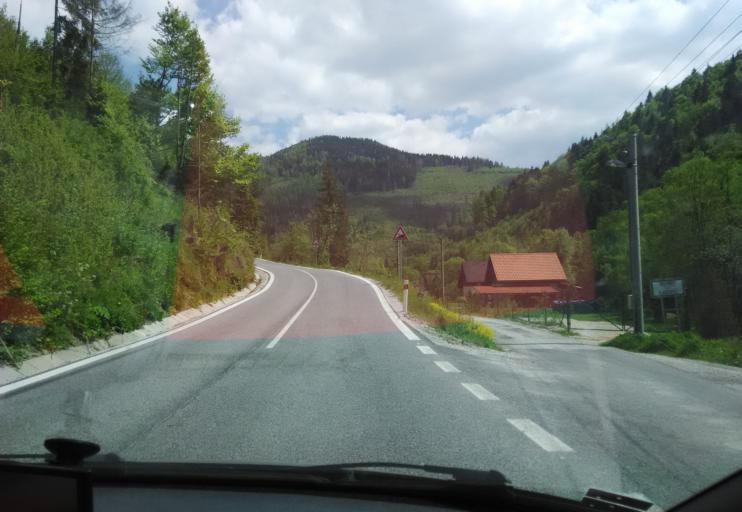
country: SK
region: Kosicky
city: Dobsina
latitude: 48.8446
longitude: 20.4285
